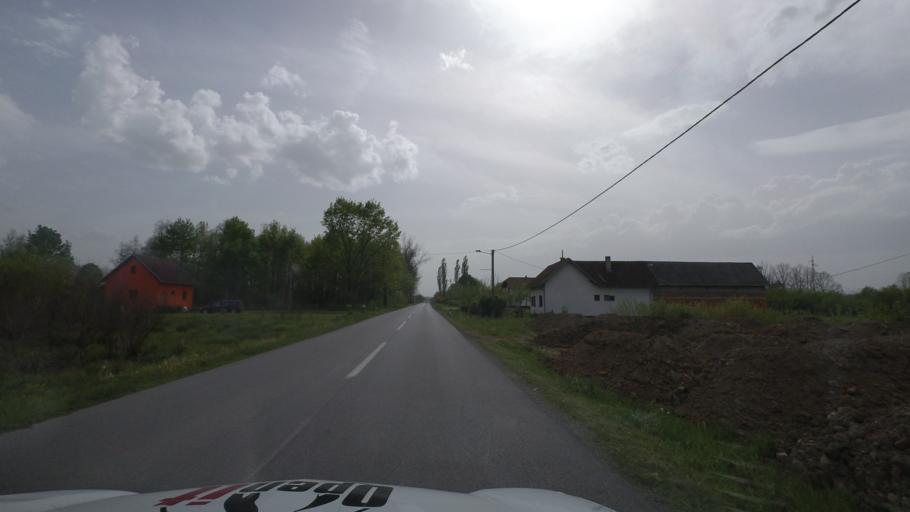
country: HR
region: Sisacko-Moslavacka
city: Glina
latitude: 45.3571
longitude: 16.1072
